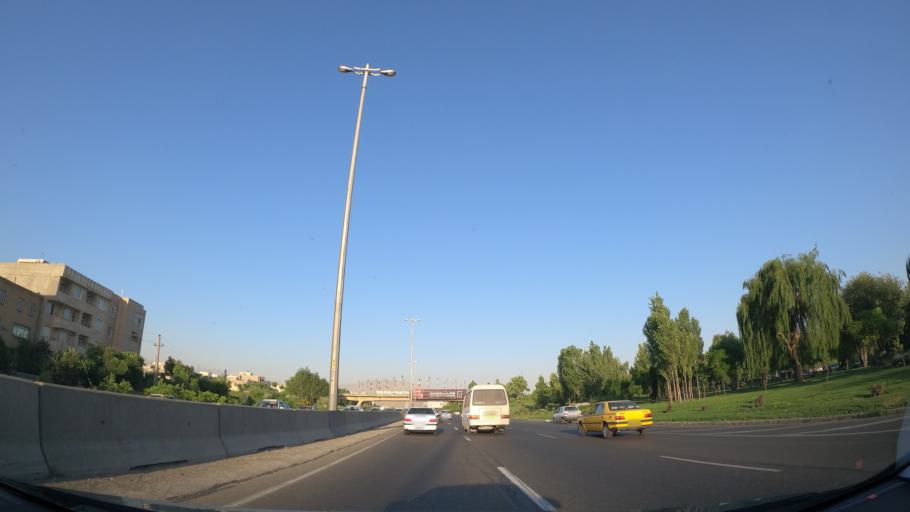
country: IR
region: Alborz
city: Karaj
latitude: 35.8182
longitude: 50.9260
